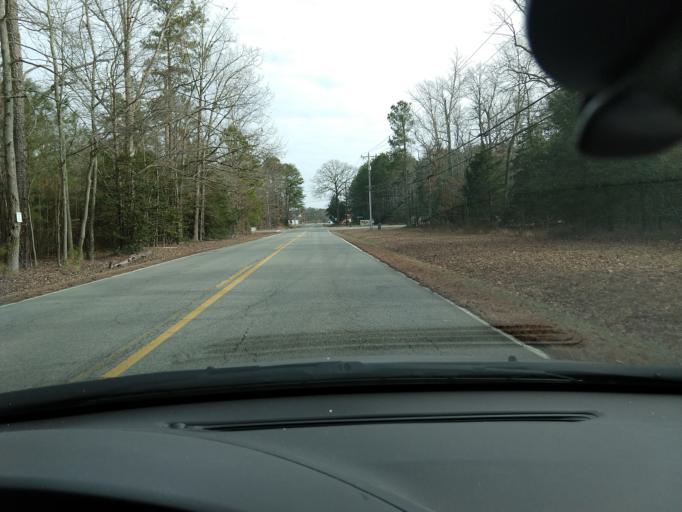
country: US
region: Virginia
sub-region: Henrico County
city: Fort Lee
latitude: 37.4459
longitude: -77.2345
